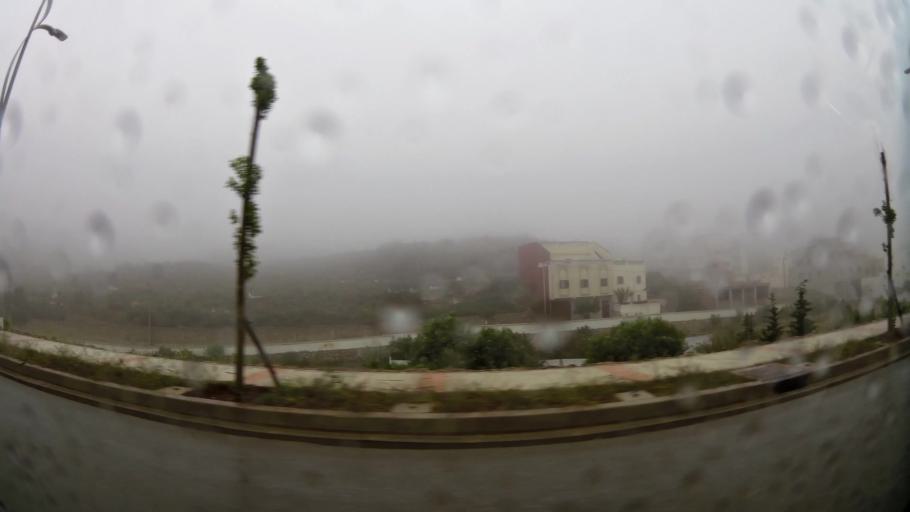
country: MA
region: Taza-Al Hoceima-Taounate
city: Tirhanimine
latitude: 35.2334
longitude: -3.9556
